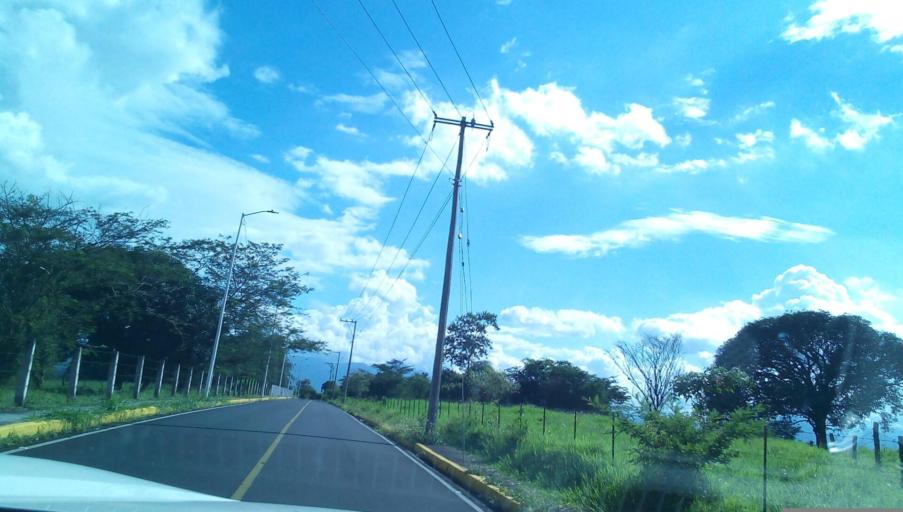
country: MX
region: Veracruz
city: Cordoba
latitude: 18.9015
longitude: -96.9231
